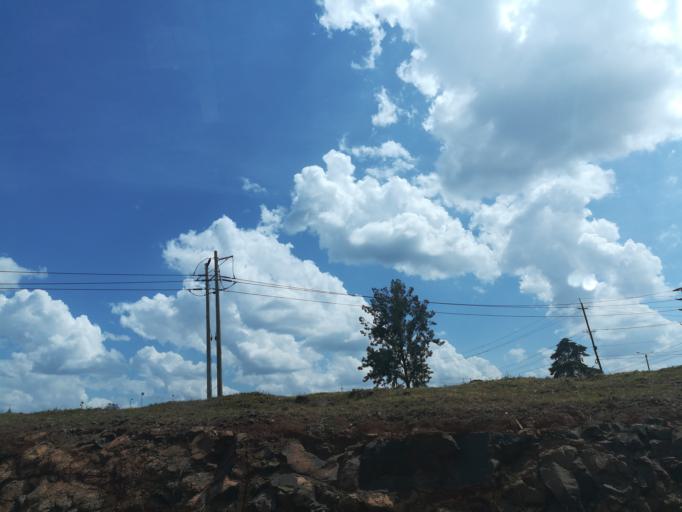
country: KE
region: Nairobi Area
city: Nairobi
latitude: -1.3258
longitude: 36.7961
